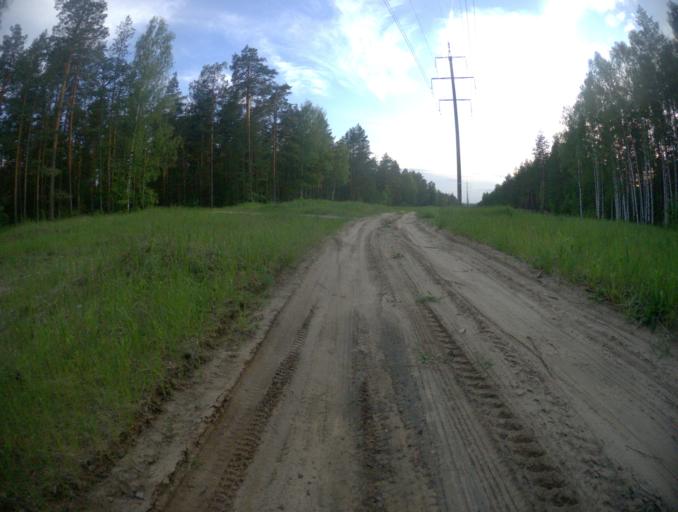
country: RU
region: Vladimir
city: Gus'-Khrustal'nyy
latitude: 55.6332
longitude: 40.6798
